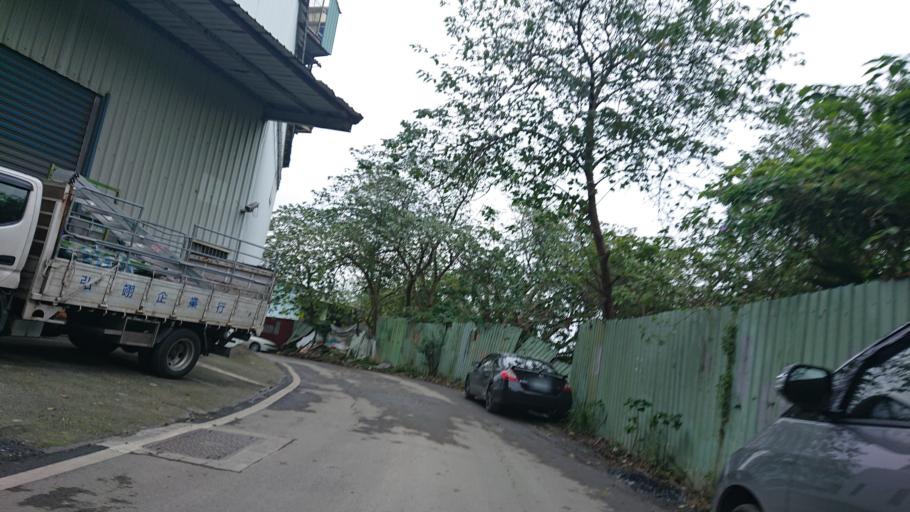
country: TW
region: Taiwan
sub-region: Taoyuan
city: Taoyuan
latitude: 24.9434
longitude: 121.3954
